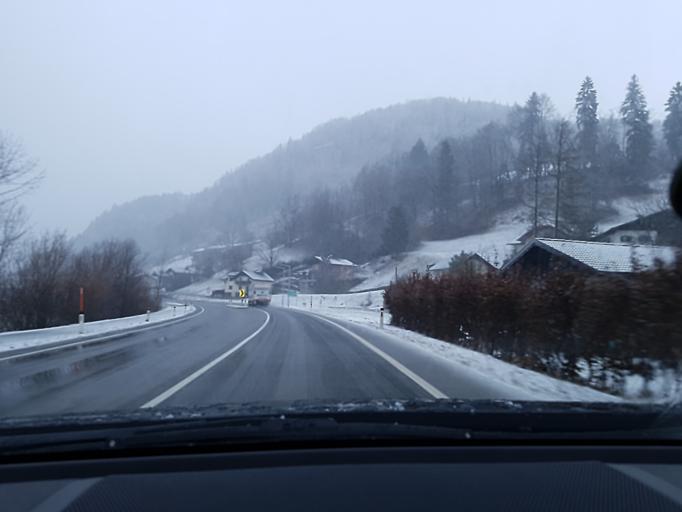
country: AT
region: Salzburg
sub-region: Politischer Bezirk Hallein
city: Scheffau am Tennengebirge
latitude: 47.5910
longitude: 13.2023
